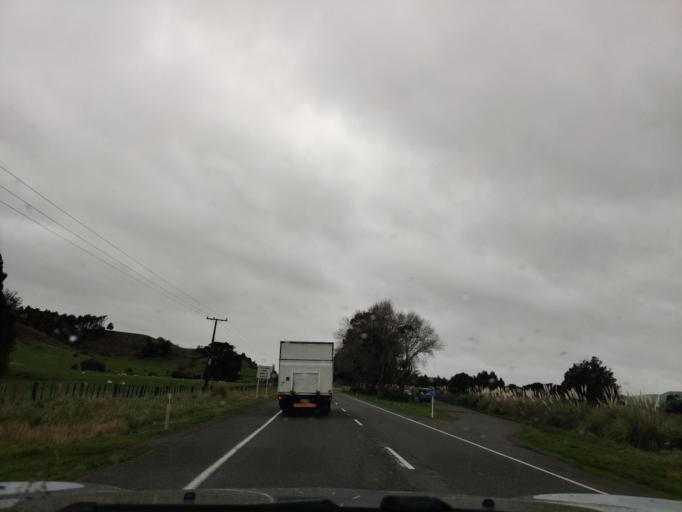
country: NZ
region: Manawatu-Wanganui
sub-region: Palmerston North City
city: Palmerston North
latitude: -40.3389
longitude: 175.8902
